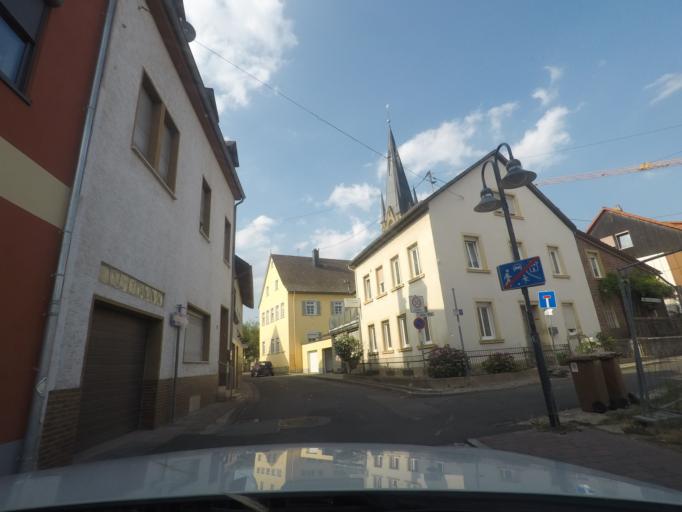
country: DE
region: Rheinland-Pfalz
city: Staudernheim
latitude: 49.7859
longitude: 7.6520
